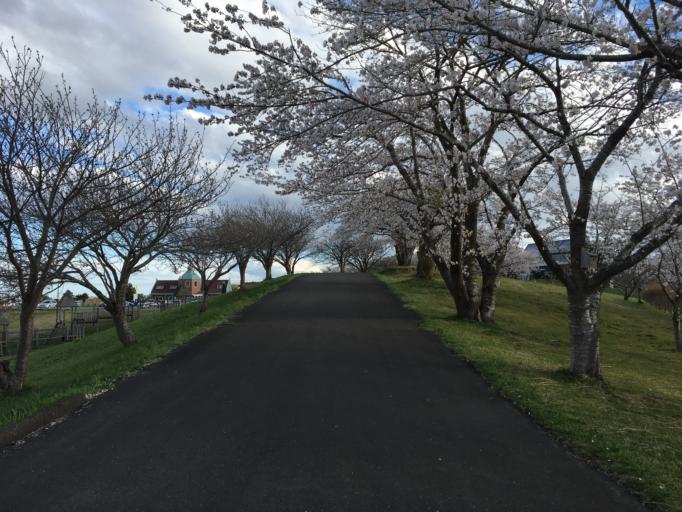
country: JP
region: Miyagi
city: Wakuya
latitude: 38.6902
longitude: 141.1340
